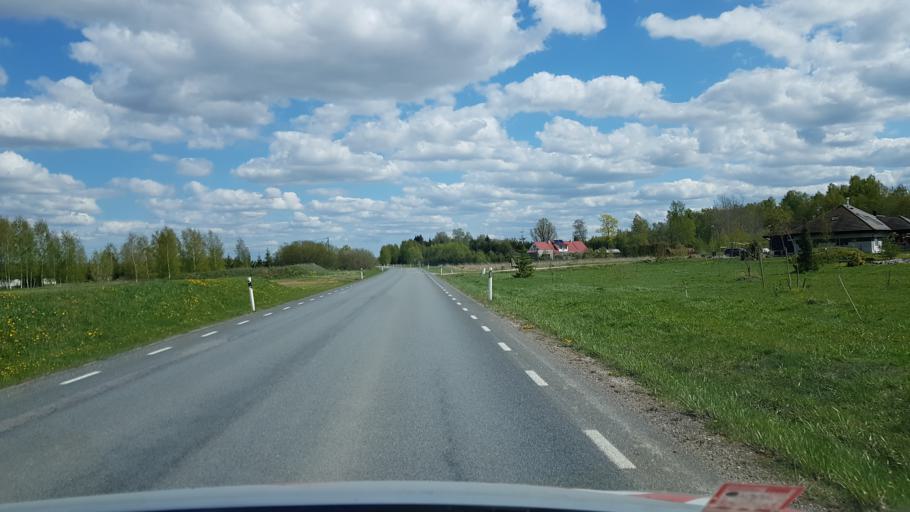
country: EE
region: Tartu
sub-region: UElenurme vald
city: Ulenurme
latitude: 58.3137
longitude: 26.6488
